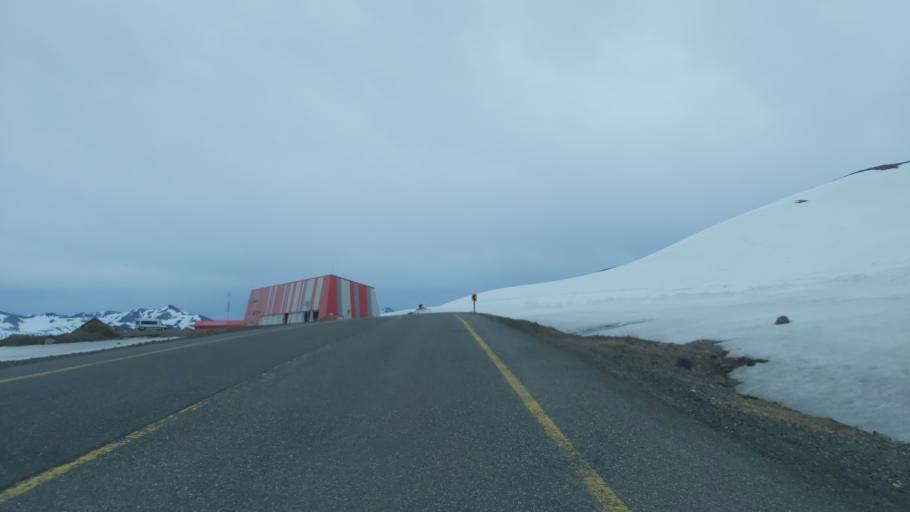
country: CL
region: Maule
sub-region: Provincia de Linares
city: Colbun
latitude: -36.0083
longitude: -70.4811
